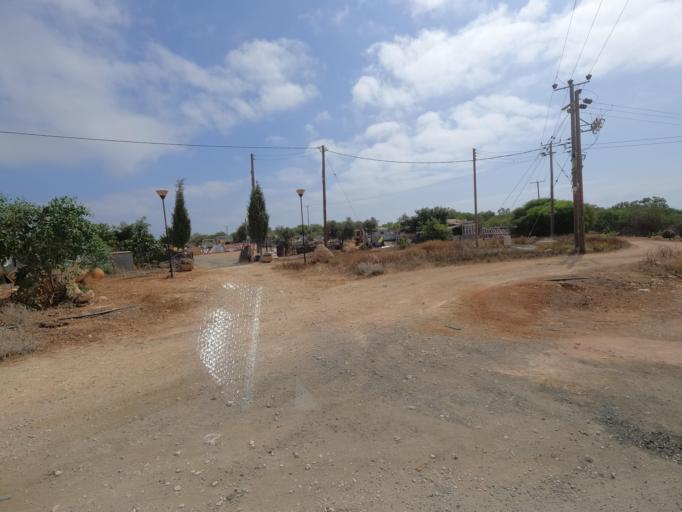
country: CY
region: Ammochostos
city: Protaras
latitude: 35.0064
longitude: 34.0433
